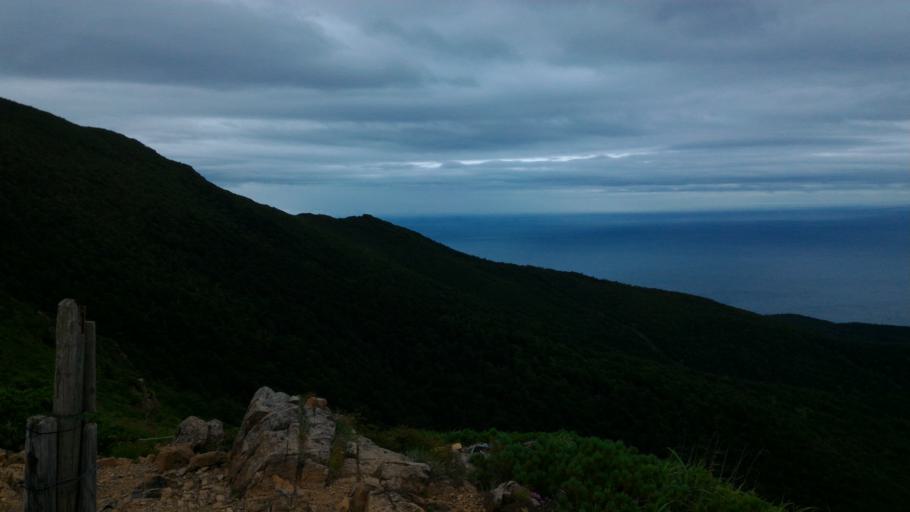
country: JP
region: Hokkaido
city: Shizunai-furukawacho
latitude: 42.1089
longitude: 143.0161
